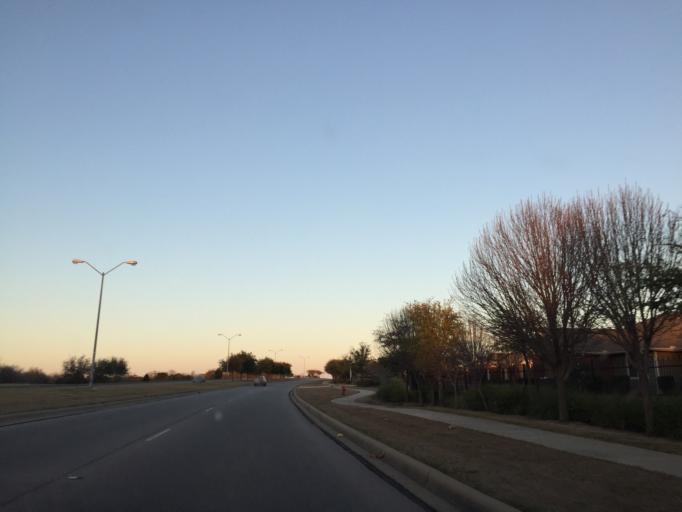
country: US
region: Texas
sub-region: Travis County
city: Pflugerville
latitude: 30.4304
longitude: -97.6225
